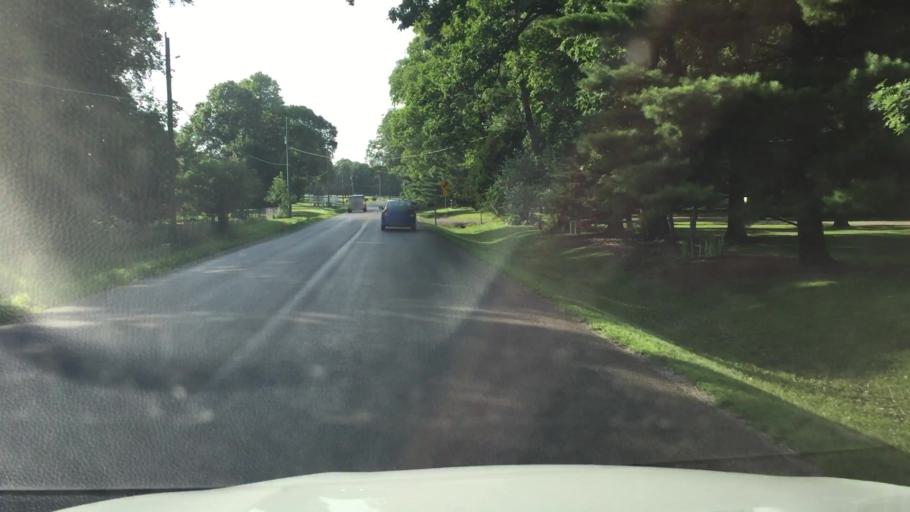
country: US
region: Iowa
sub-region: Linn County
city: Ely
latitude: 41.8204
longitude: -91.6227
